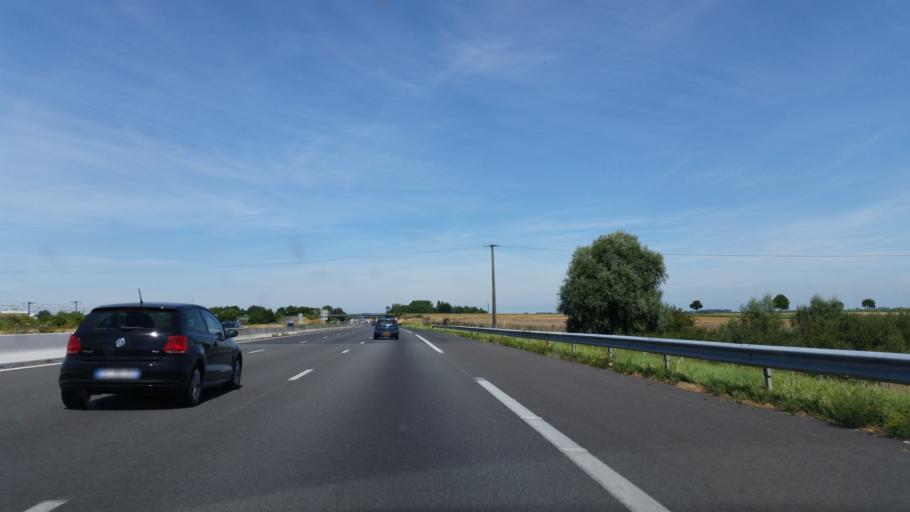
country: FR
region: Nord-Pas-de-Calais
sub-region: Departement du Pas-de-Calais
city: Bapaume
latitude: 50.0929
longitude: 2.8715
